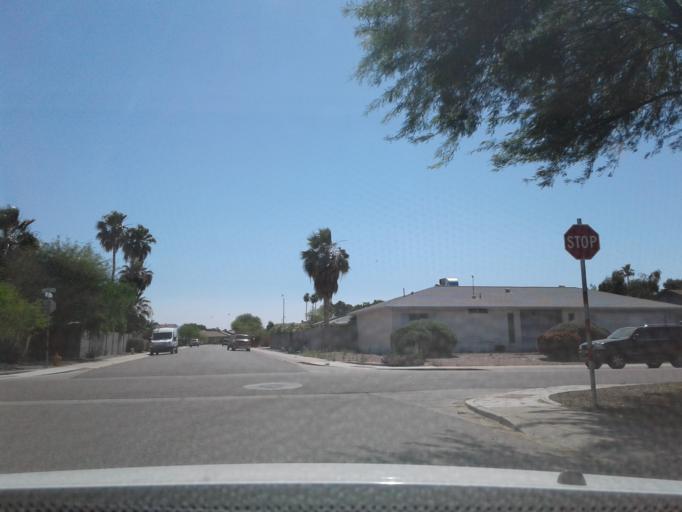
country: US
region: Arizona
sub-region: Maricopa County
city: Paradise Valley
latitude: 33.5990
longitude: -112.0004
